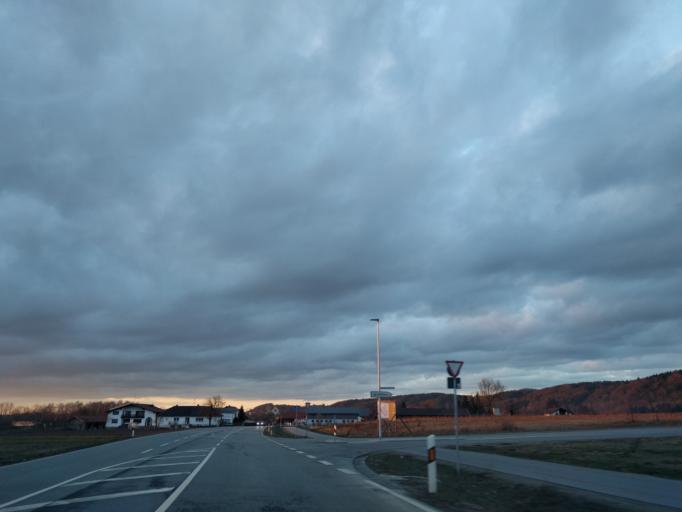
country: DE
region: Bavaria
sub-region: Lower Bavaria
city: Hofkirchen
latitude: 48.6981
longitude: 13.1156
